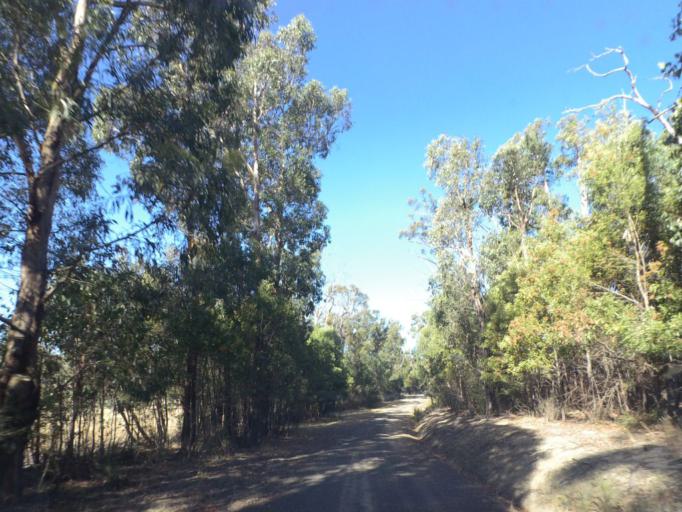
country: AU
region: Victoria
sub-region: Murrindindi
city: Kinglake West
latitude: -37.4602
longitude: 145.3896
